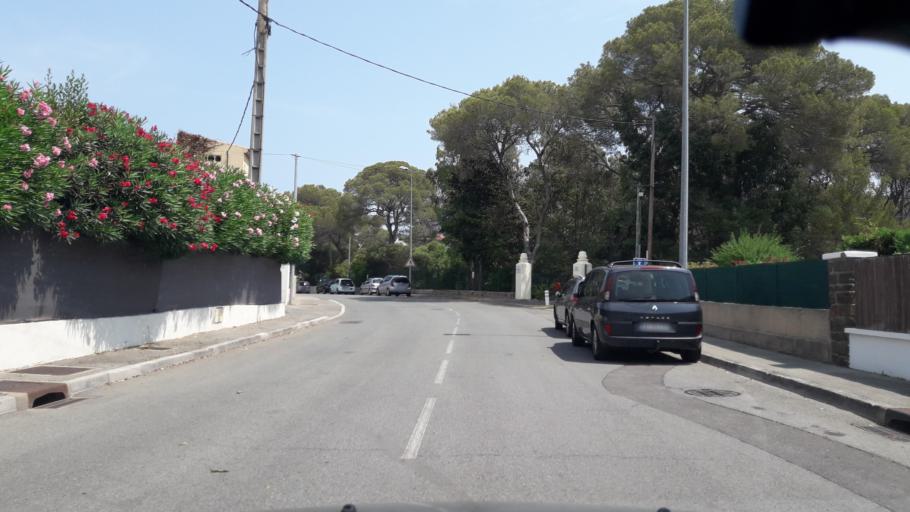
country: FR
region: Provence-Alpes-Cote d'Azur
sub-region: Departement du Var
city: Saint-Raphael
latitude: 43.4196
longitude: 6.8021
